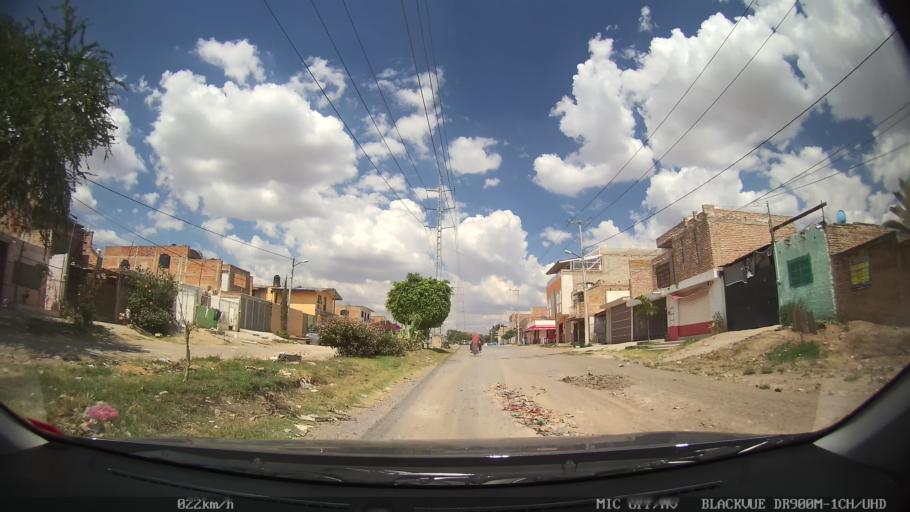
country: MX
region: Jalisco
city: Tlaquepaque
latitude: 20.6670
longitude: -103.2574
